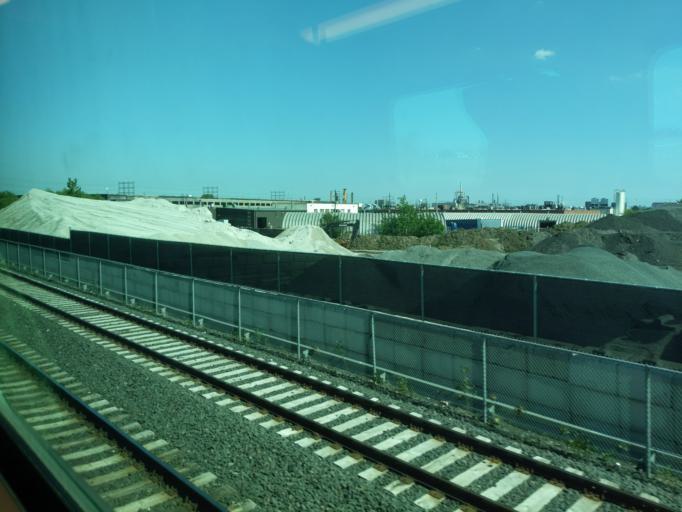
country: CA
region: Ontario
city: Etobicoke
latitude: 43.7057
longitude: -79.5947
